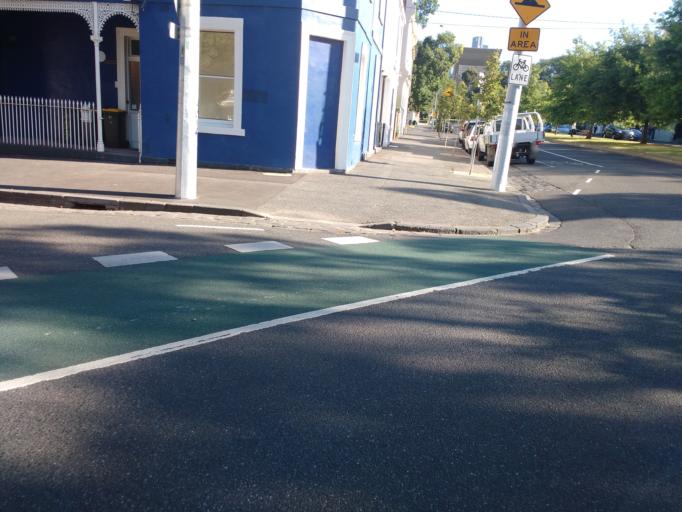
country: AU
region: Victoria
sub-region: Yarra
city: Fitzroy
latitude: -37.7993
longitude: 144.9728
